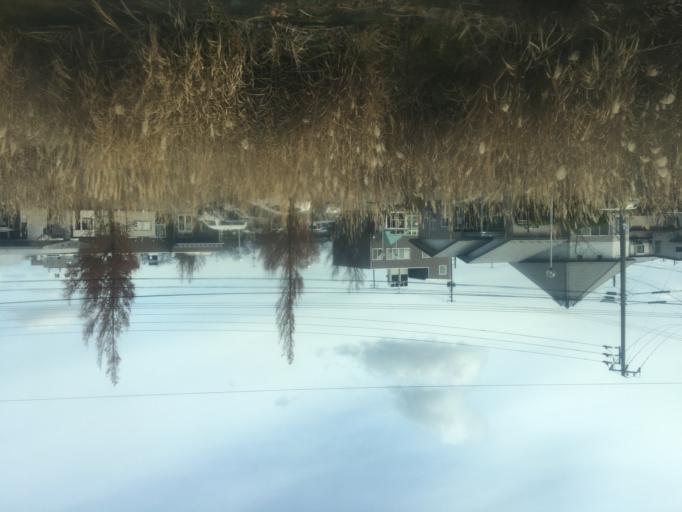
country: JP
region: Akita
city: Tenno
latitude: 39.8696
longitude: 140.0624
